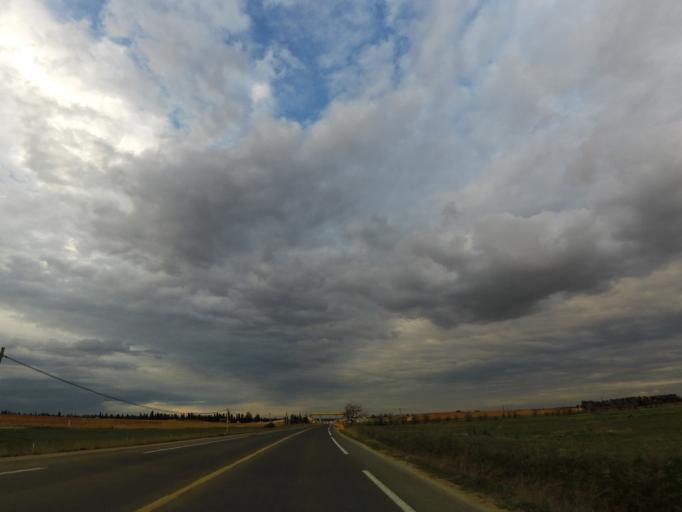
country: FR
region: Languedoc-Roussillon
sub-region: Departement du Gard
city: Vestric-et-Candiac
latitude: 43.7212
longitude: 4.2695
